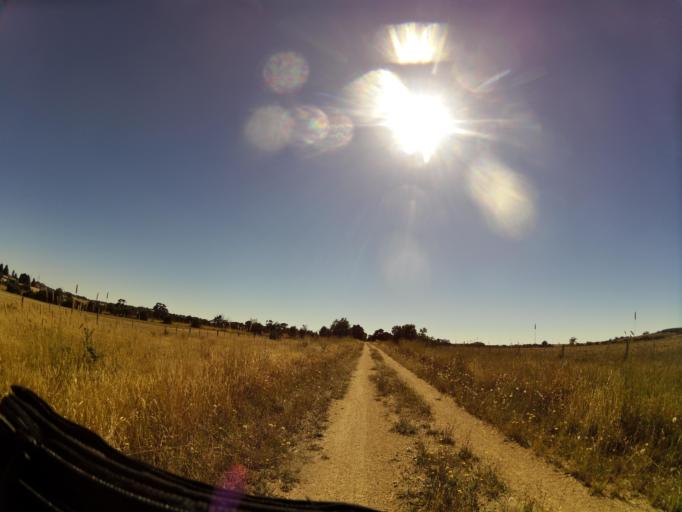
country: AU
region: Victoria
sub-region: Ballarat North
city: Delacombe
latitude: -37.6840
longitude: 143.4152
